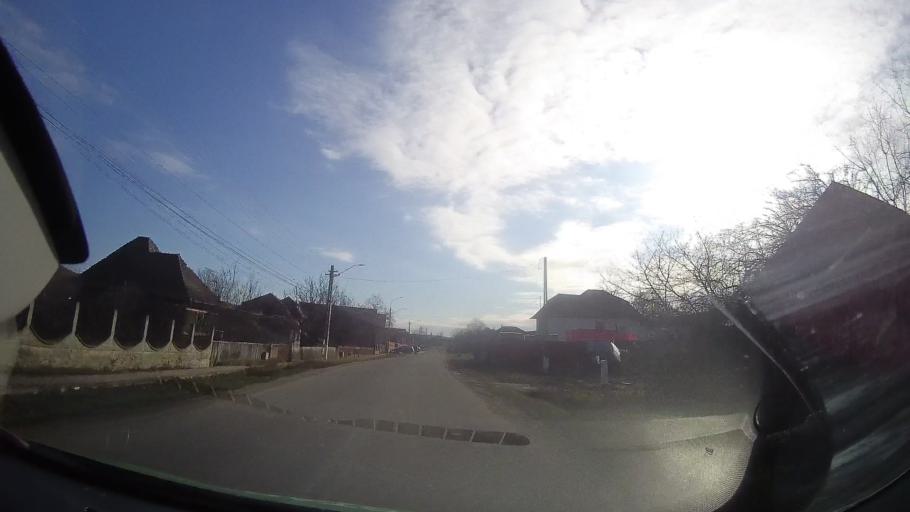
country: RO
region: Mures
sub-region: Comuna Valea Larga
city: Valea Larga
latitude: 46.6191
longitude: 24.0790
